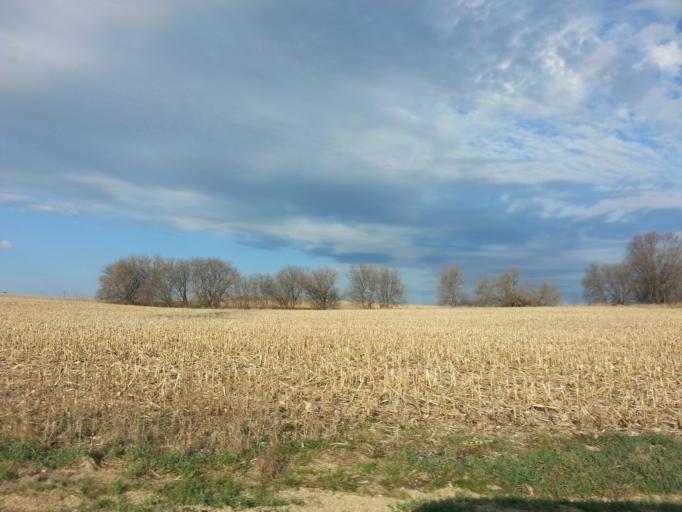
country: US
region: Minnesota
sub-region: Dakota County
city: Hastings
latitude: 44.8230
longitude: -92.8416
